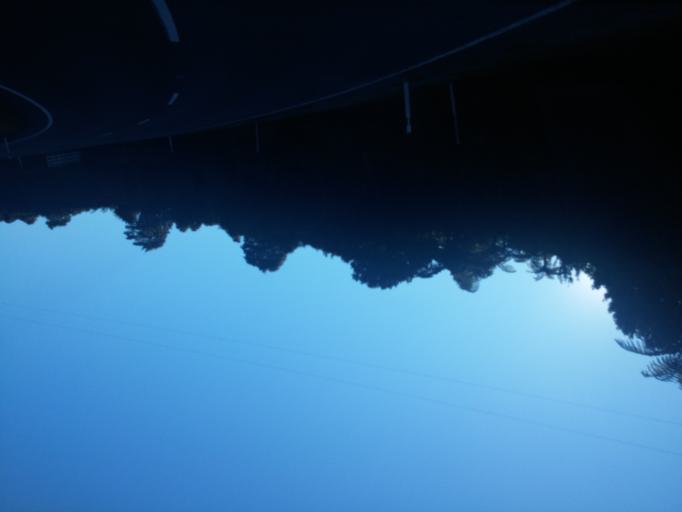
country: NZ
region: West Coast
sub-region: Grey District
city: Greymouth
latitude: -42.0985
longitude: 171.3416
